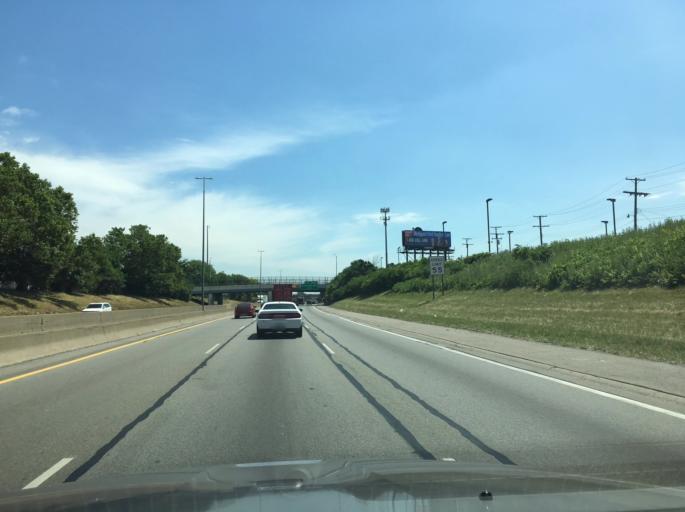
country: US
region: Michigan
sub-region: Wayne County
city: Dearborn
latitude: 42.3309
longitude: -83.1474
